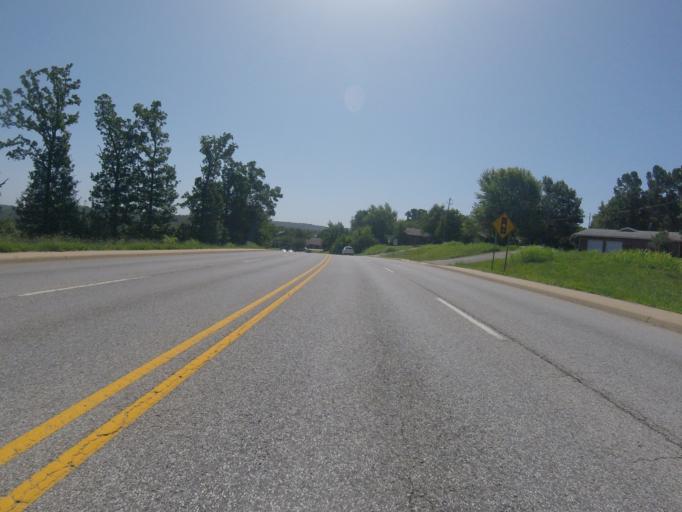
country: US
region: Arkansas
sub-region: Washington County
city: Fayetteville
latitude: 36.0780
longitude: -94.1780
